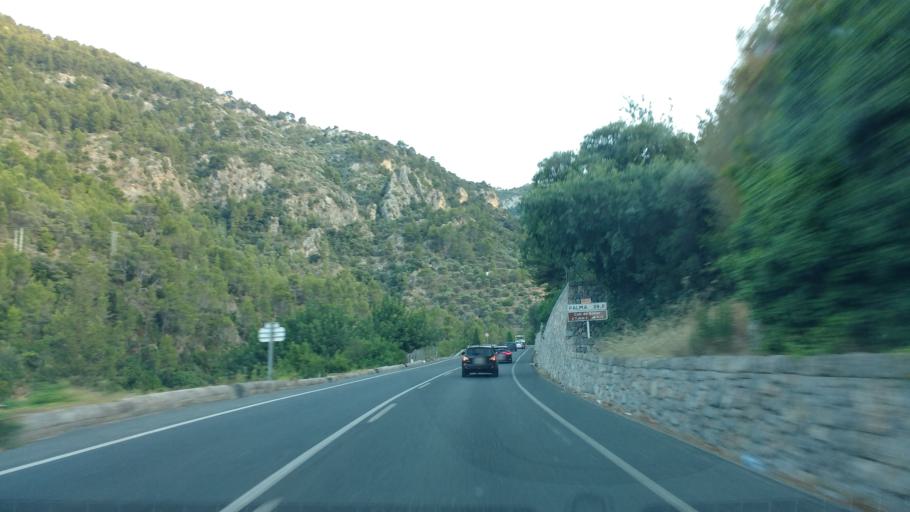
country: ES
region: Balearic Islands
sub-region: Illes Balears
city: Soller
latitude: 39.7594
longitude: 2.7116
